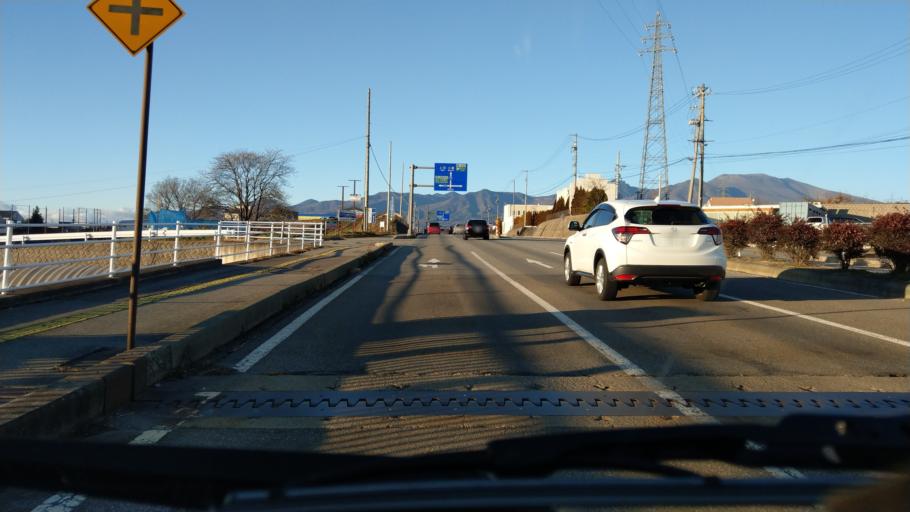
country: JP
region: Nagano
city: Saku
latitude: 36.2632
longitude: 138.4671
